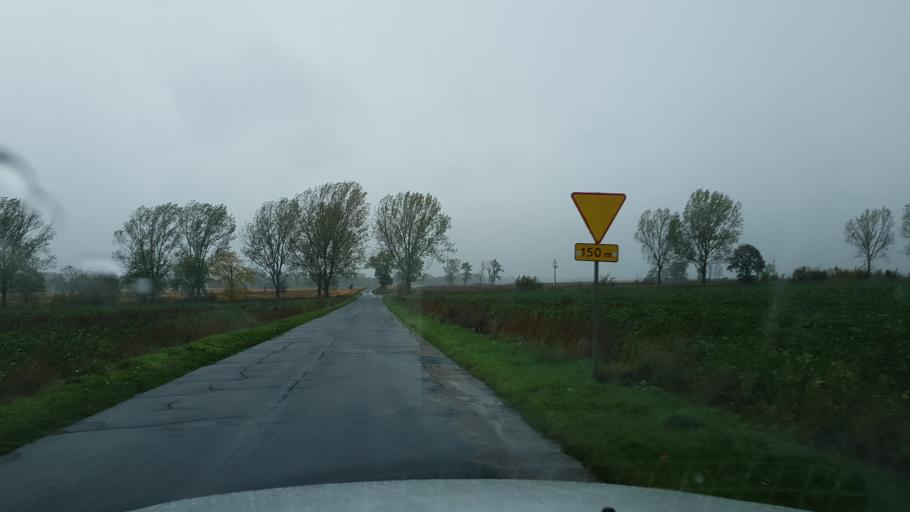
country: PL
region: West Pomeranian Voivodeship
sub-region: Powiat pyrzycki
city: Kozielice
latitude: 53.1712
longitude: 14.8177
